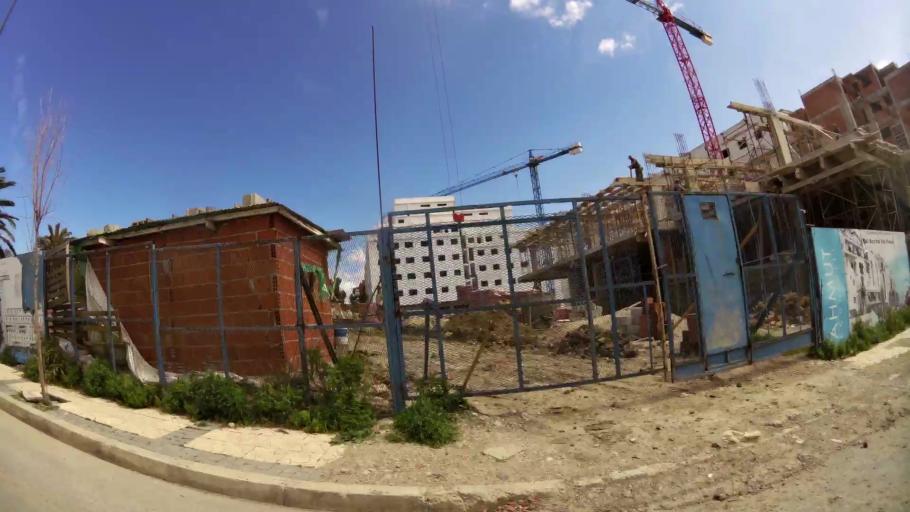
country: MA
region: Tanger-Tetouan
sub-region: Tanger-Assilah
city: Tangier
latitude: 35.7650
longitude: -5.8397
